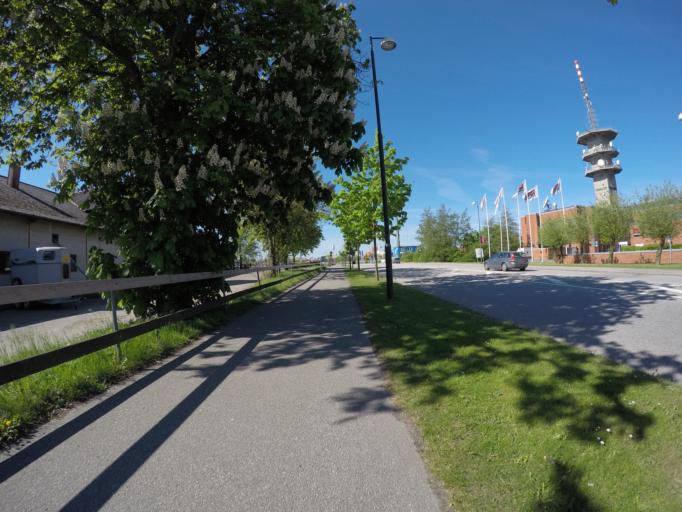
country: SE
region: Skane
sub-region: Malmo
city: Oxie
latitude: 55.5735
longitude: 13.0595
